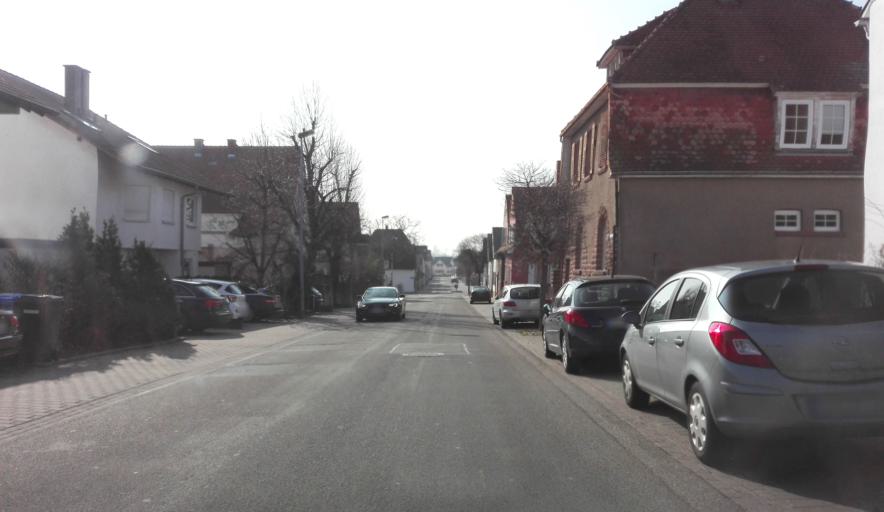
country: DE
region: Rheinland-Pfalz
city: Dirmstein
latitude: 49.5669
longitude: 8.2496
